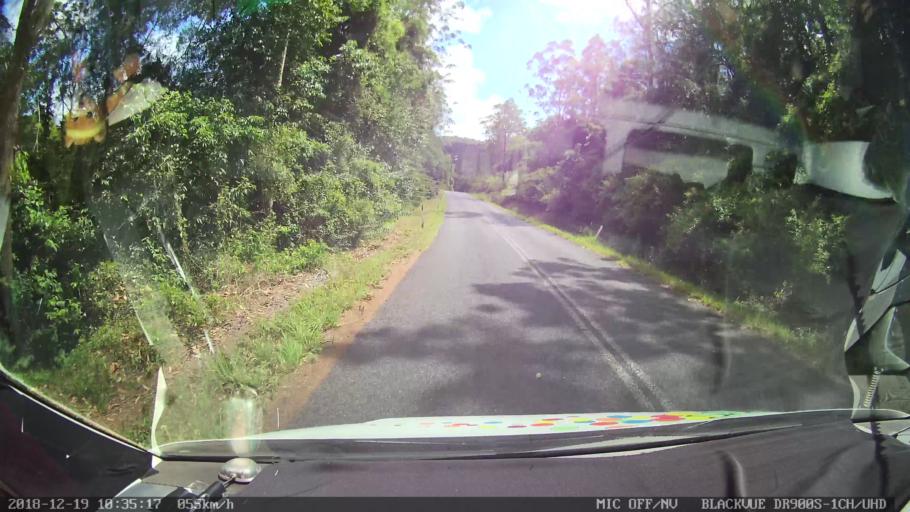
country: AU
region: New South Wales
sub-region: Lismore Municipality
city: Larnook
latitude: -28.5773
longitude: 153.1352
